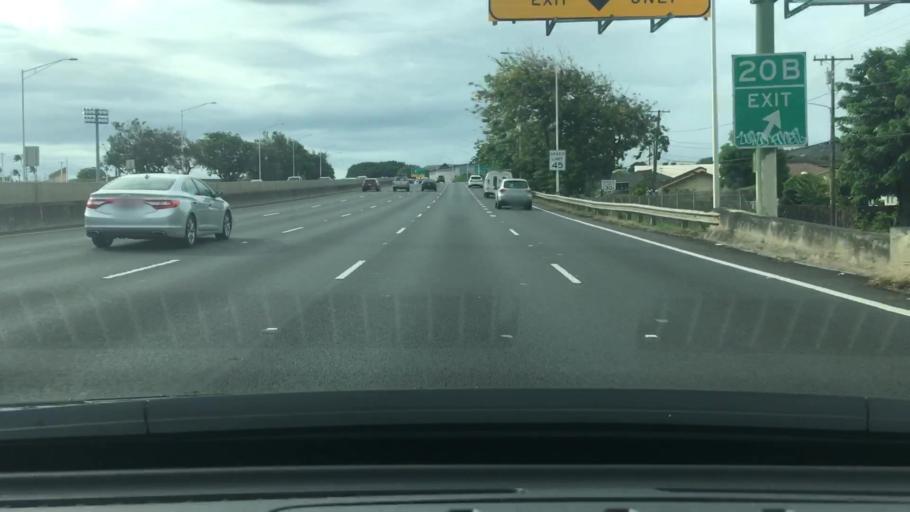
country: US
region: Hawaii
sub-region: Honolulu County
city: Honolulu
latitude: 21.3286
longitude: -157.8687
